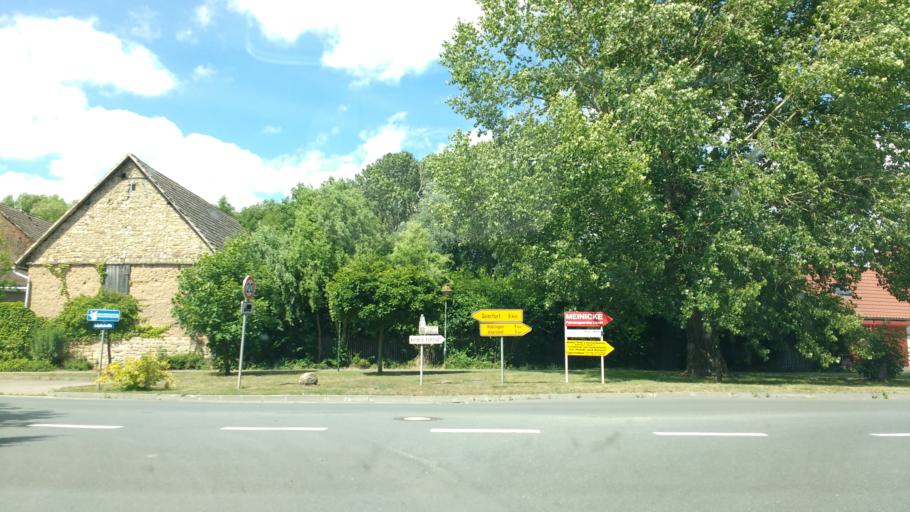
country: DE
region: Saxony-Anhalt
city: Farnstadt
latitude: 51.4284
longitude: 11.5694
